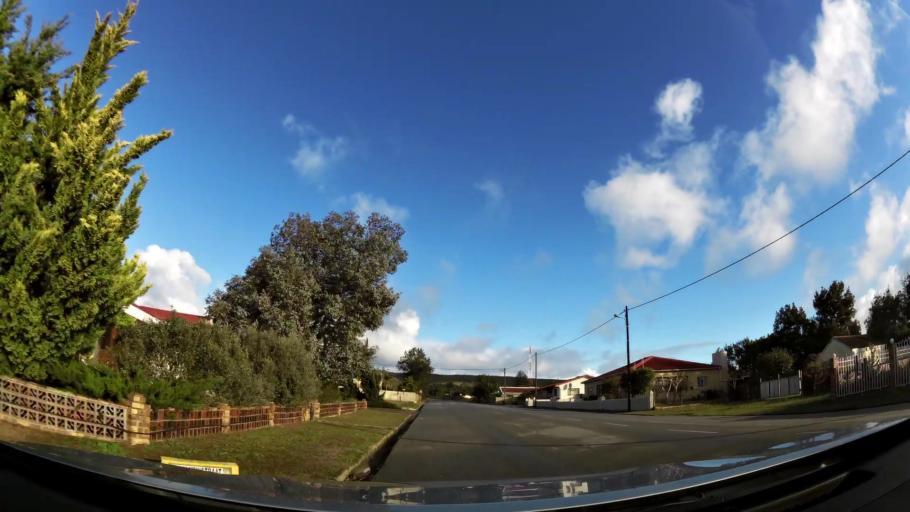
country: ZA
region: Western Cape
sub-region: Eden District Municipality
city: Riversdale
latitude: -34.2076
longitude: 21.5864
